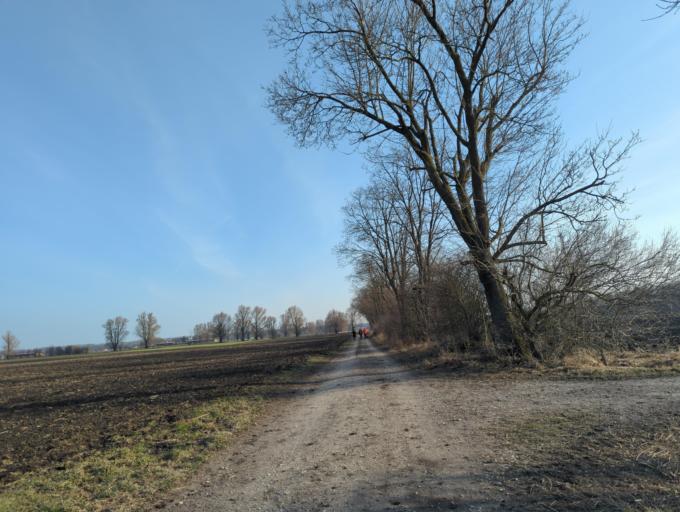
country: DE
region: Bavaria
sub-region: Swabia
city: Leipheim
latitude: 48.4744
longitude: 10.2022
